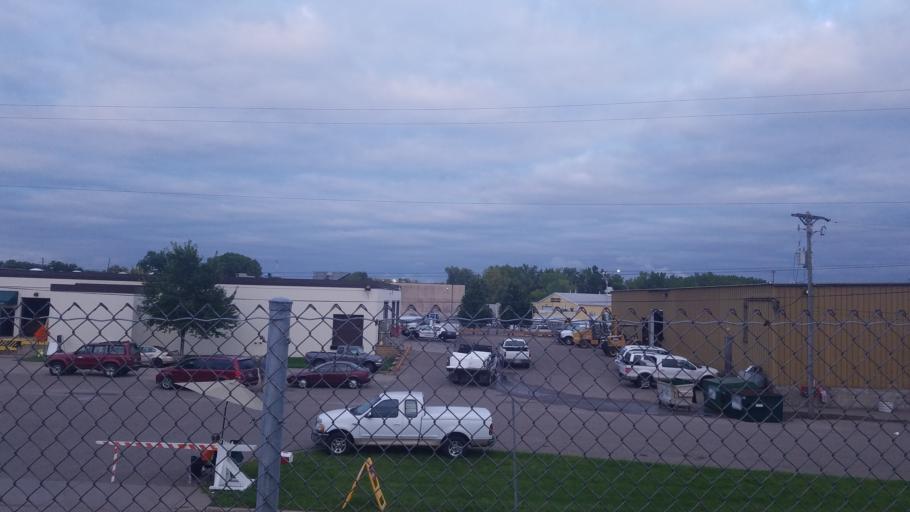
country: US
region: Minnesota
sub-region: Ramsey County
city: Falcon Heights
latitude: 44.9757
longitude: -93.1810
